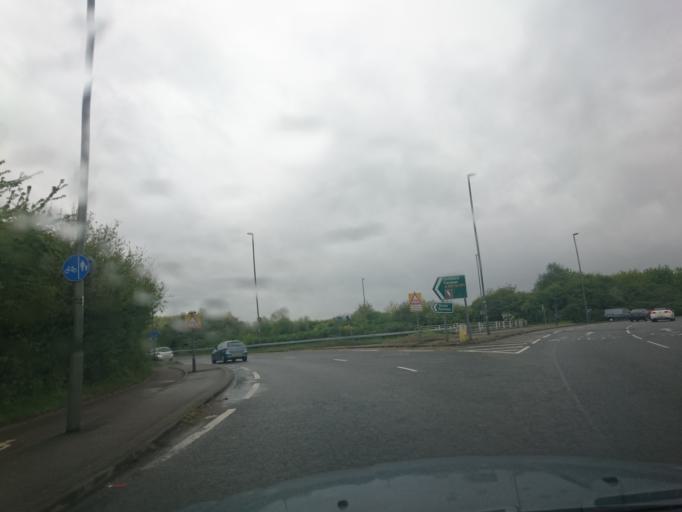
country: GB
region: England
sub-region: Surrey
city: Seale
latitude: 51.2418
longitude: -0.7357
